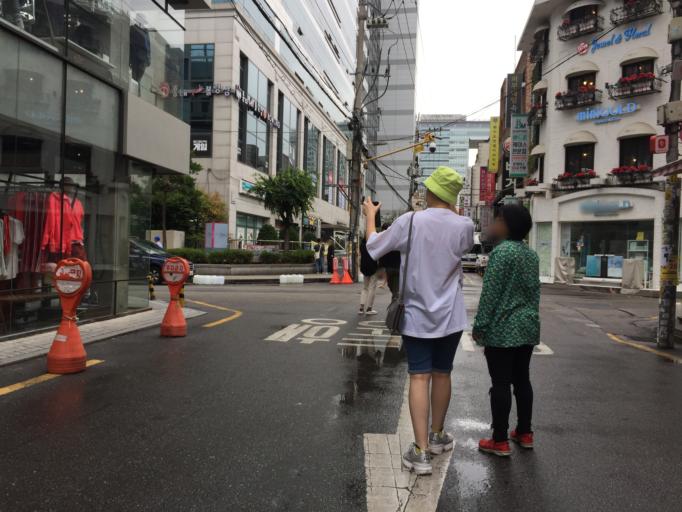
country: KR
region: Seoul
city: Seoul
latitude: 37.5556
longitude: 126.9231
